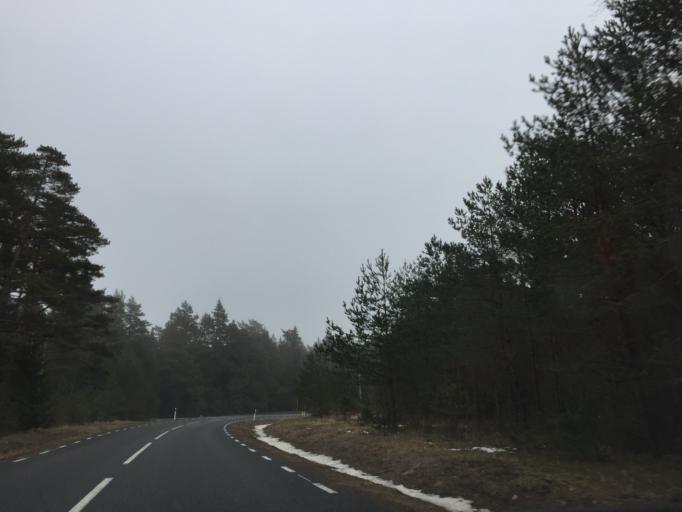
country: EE
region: Saare
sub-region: Kuressaare linn
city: Kuressaare
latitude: 58.4695
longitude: 22.0314
